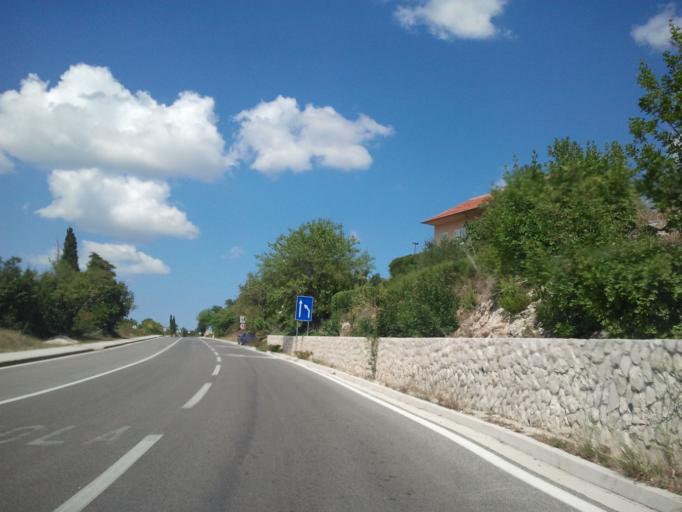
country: HR
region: Zadarska
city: Benkovac
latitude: 44.0379
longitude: 15.6201
